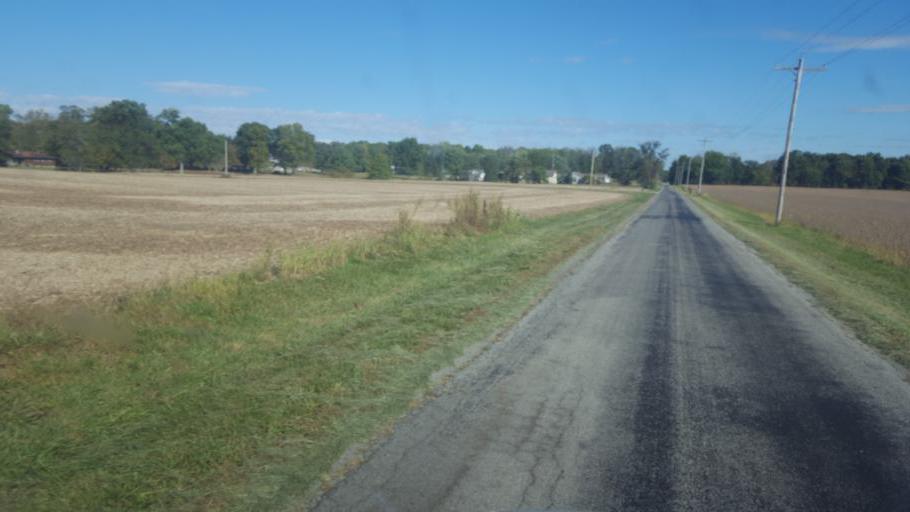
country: US
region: Ohio
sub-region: Wyandot County
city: Upper Sandusky
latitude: 40.7457
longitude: -83.2074
